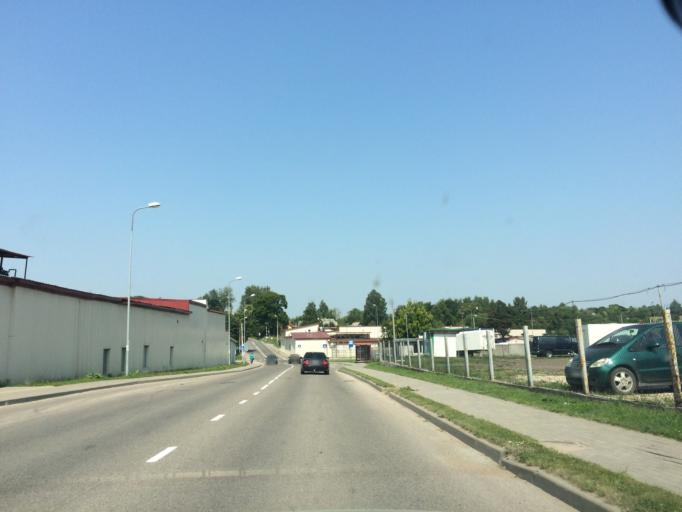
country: LV
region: Rezekne
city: Rezekne
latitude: 56.5124
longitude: 27.3248
